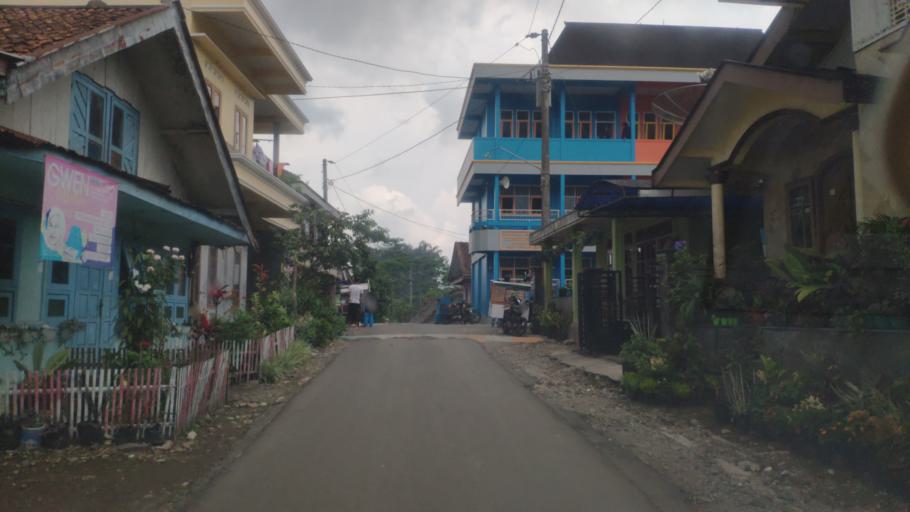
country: ID
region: Central Java
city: Wonosobo
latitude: -7.2453
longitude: 109.7762
